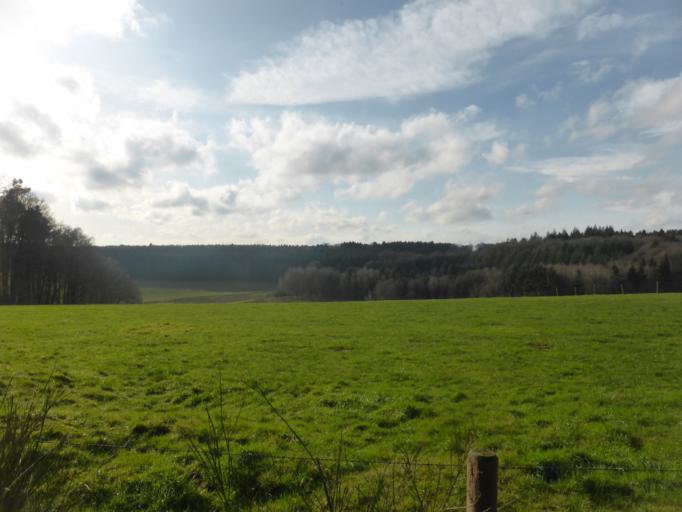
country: LU
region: Diekirch
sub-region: Canton de Redange
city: Grosbous
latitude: 49.8419
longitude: 5.9681
